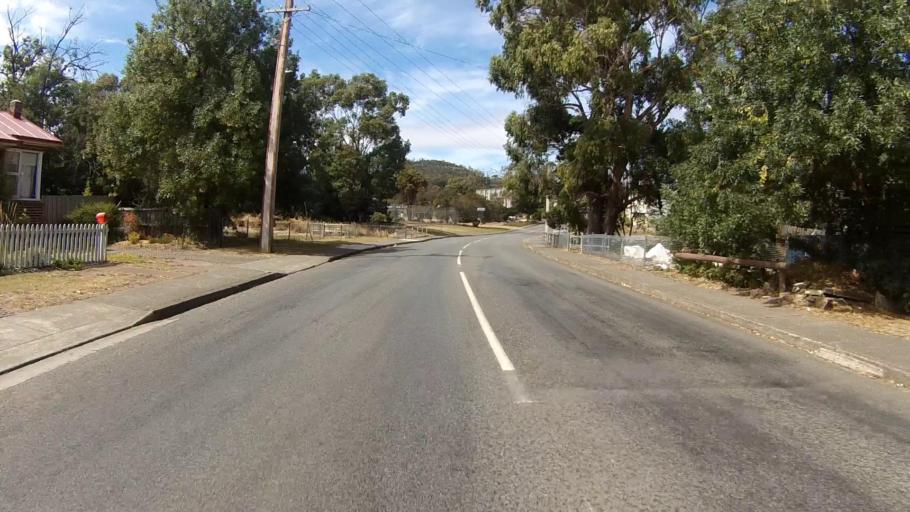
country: AU
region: Tasmania
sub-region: Clarence
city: Lindisfarne
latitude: -42.8098
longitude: 147.3509
